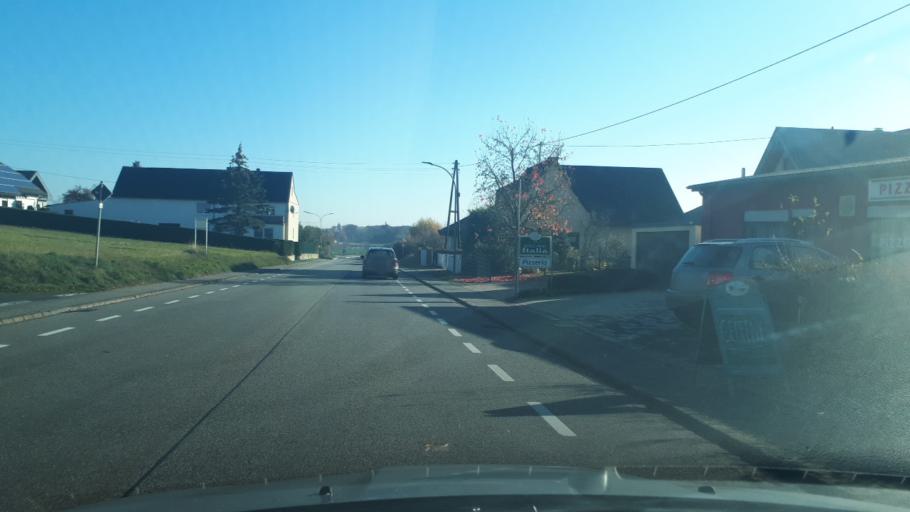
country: DE
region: Rheinland-Pfalz
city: Buchel
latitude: 50.1715
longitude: 7.0853
